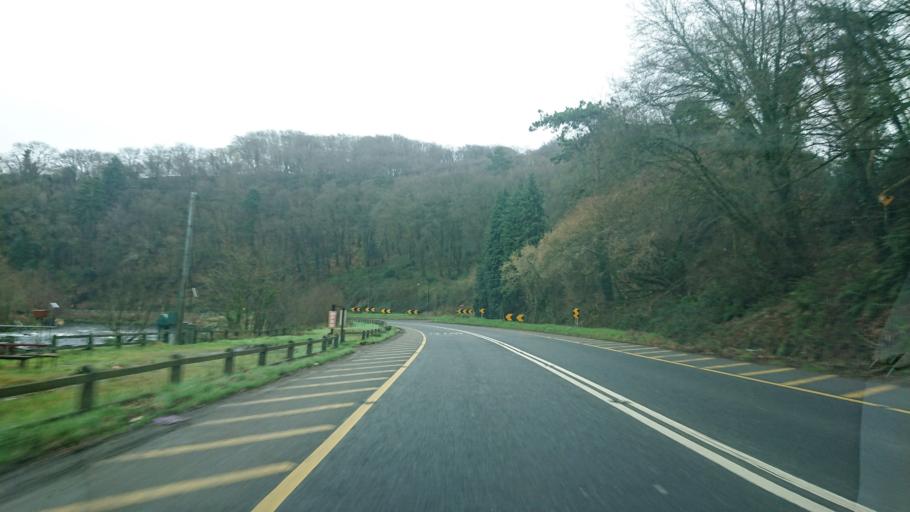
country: IE
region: Munster
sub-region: County Cork
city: Bandon
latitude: 51.7655
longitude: -8.6834
